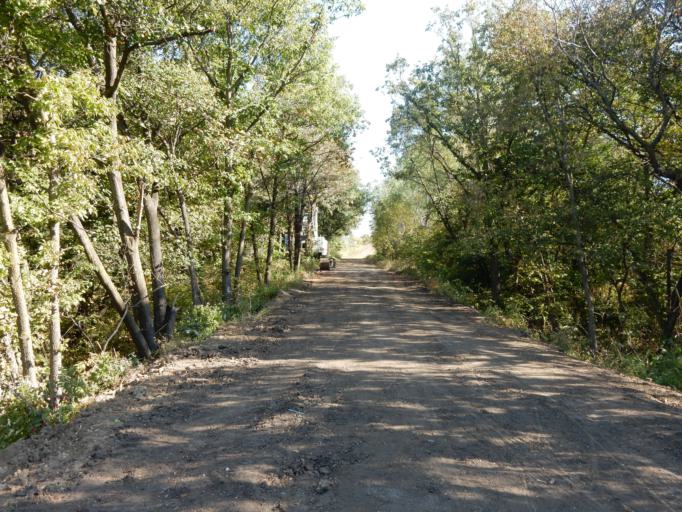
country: US
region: Nebraska
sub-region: Lancaster County
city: Lincoln
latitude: 40.7448
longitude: -96.7115
